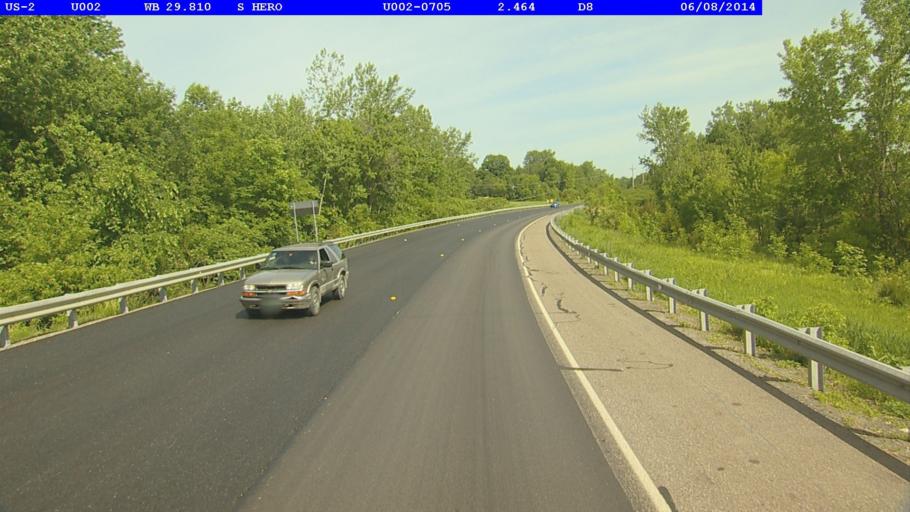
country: US
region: New York
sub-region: Clinton County
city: Cumberland Head
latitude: 44.6468
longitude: -73.3144
